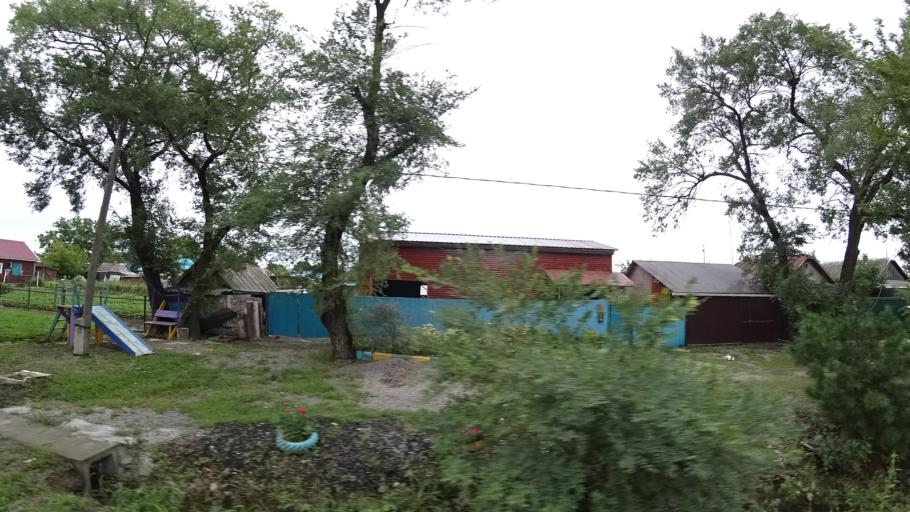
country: RU
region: Primorskiy
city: Chernigovka
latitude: 44.3469
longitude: 132.5630
